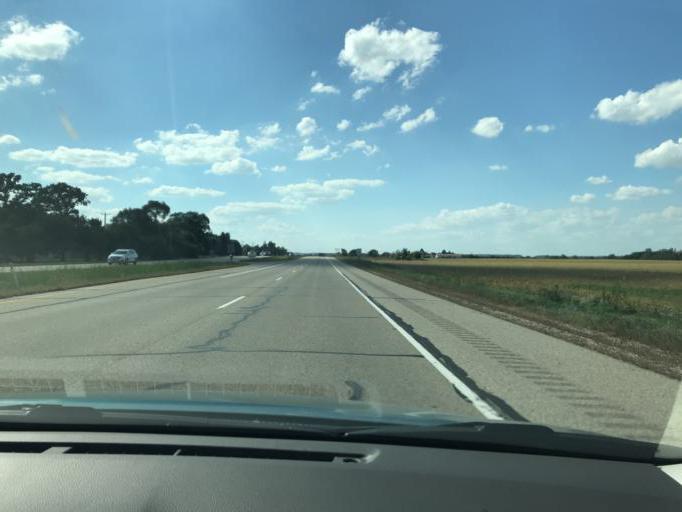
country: US
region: Wisconsin
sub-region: Walworth County
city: Pell Lake
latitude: 42.5968
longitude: -88.3662
